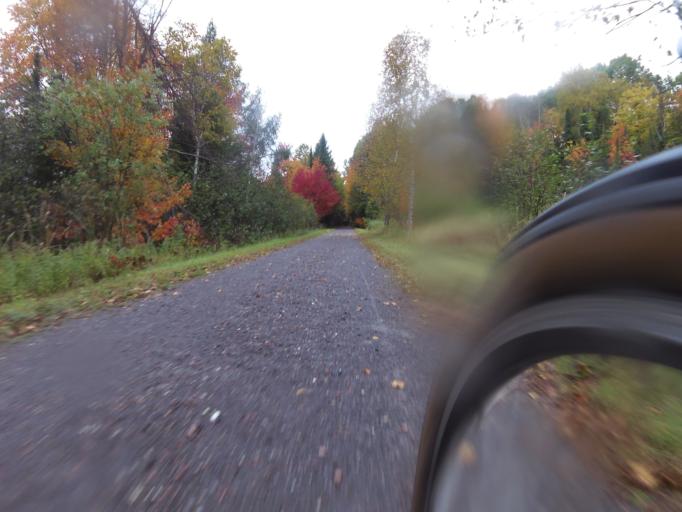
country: CA
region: Quebec
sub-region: Outaouais
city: Shawville
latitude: 45.6679
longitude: -76.5389
